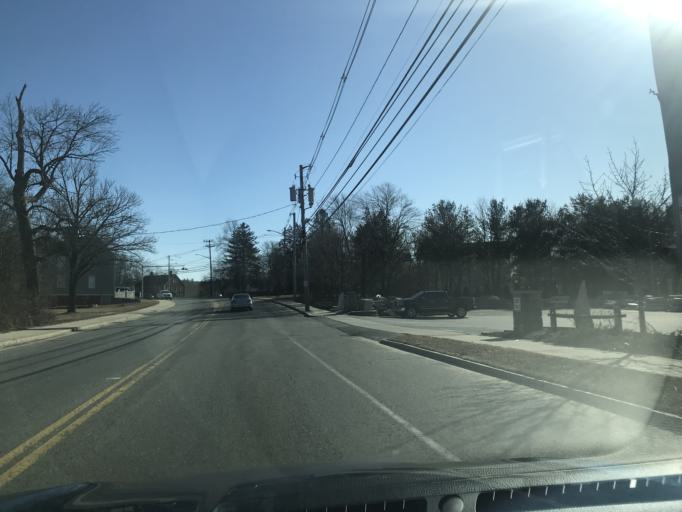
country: US
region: Massachusetts
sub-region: Essex County
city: Groveland
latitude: 42.7206
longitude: -70.9865
